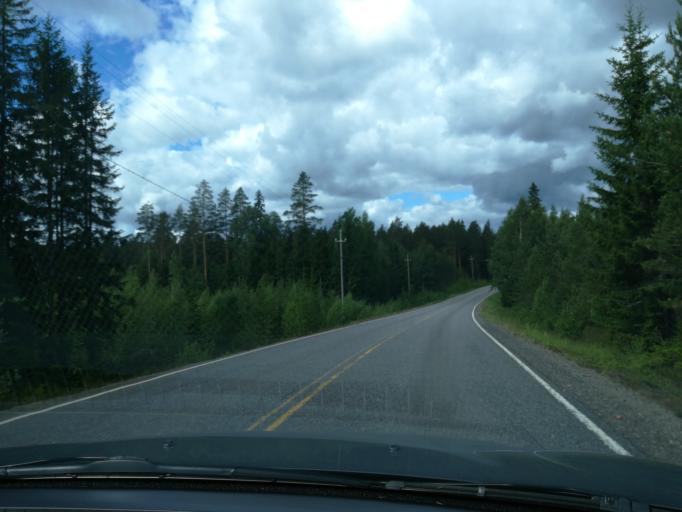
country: FI
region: Southern Savonia
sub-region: Mikkeli
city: Maentyharju
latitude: 61.3619
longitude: 27.0360
